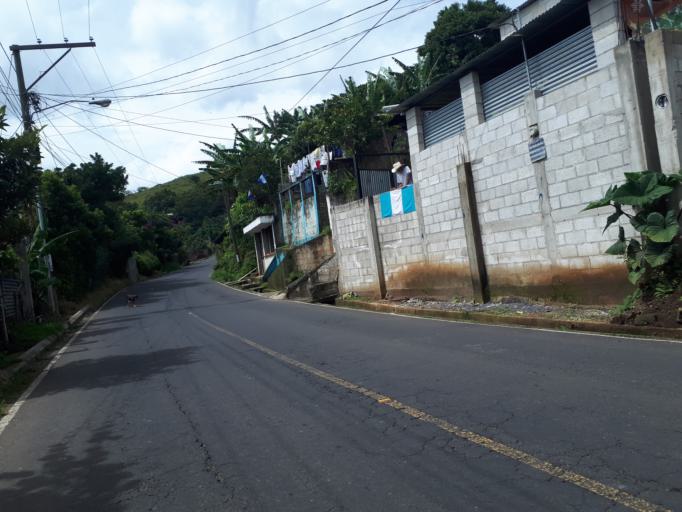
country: GT
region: Guatemala
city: Villa Canales
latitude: 14.4605
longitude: -90.5130
